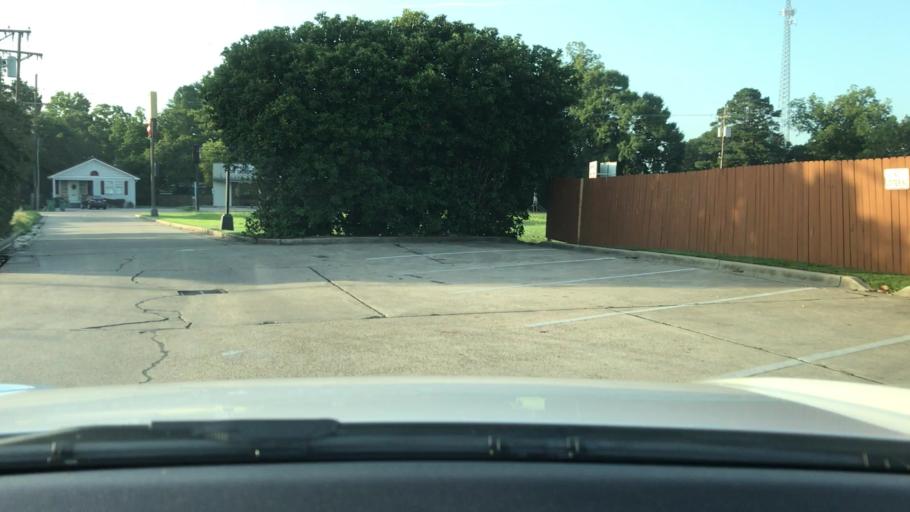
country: US
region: Louisiana
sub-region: Iberville Parish
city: Plaquemine
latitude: 30.2812
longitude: -91.2289
